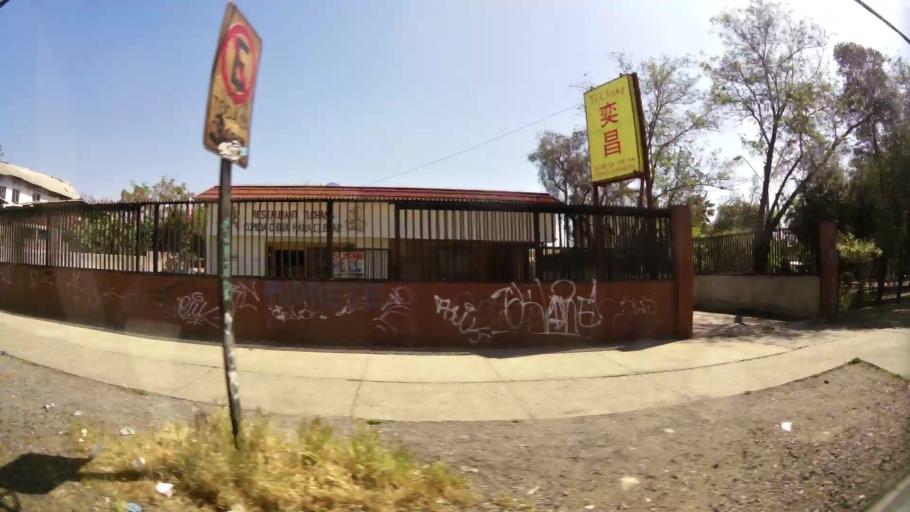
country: CL
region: Santiago Metropolitan
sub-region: Provincia de Santiago
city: Lo Prado
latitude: -33.4987
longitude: -70.7447
